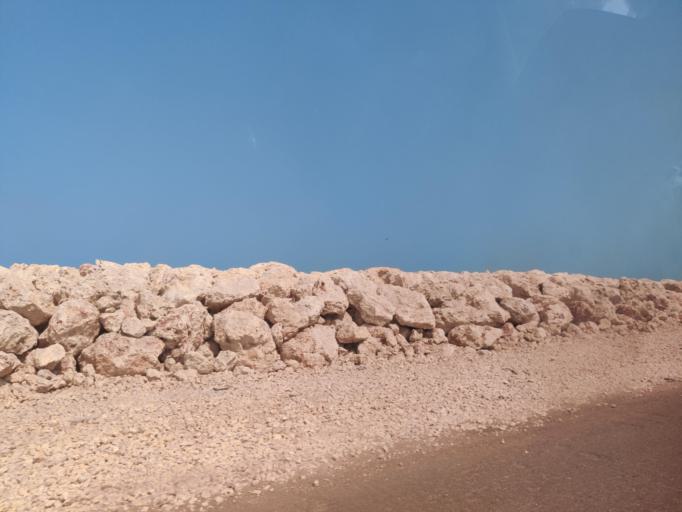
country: CO
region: Bolivar
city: Turbana
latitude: 10.1885
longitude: -75.6393
